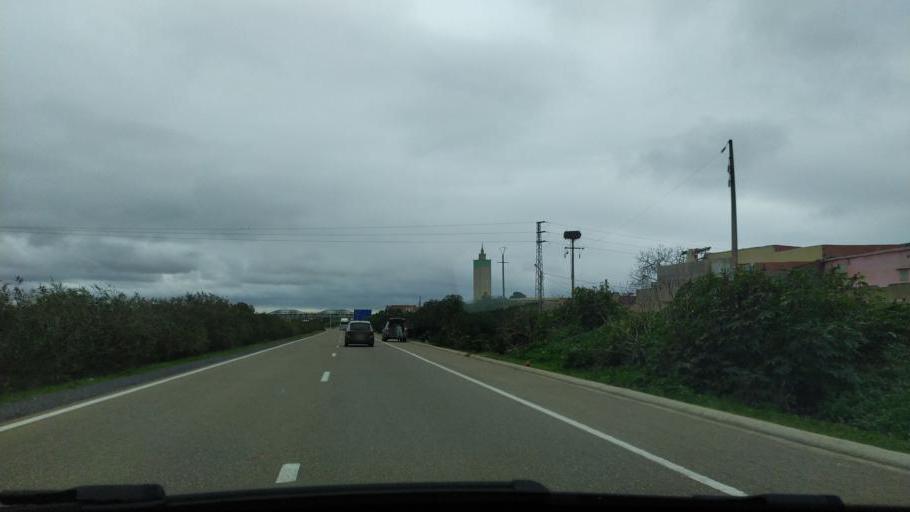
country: MA
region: Gharb-Chrarda-Beni Hssen
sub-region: Kenitra Province
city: Lalla Mimouna
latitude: 34.8663
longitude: -6.2193
